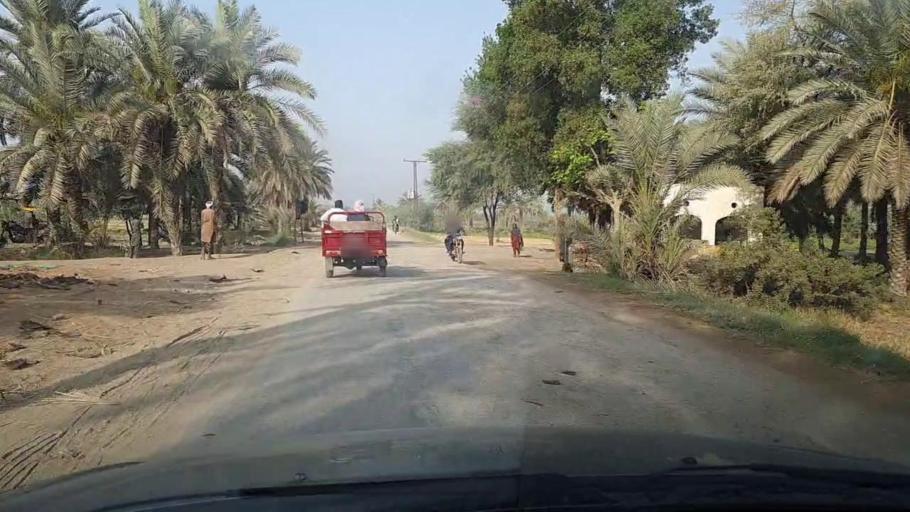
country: PK
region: Sindh
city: Pir jo Goth
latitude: 27.5646
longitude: 68.5740
